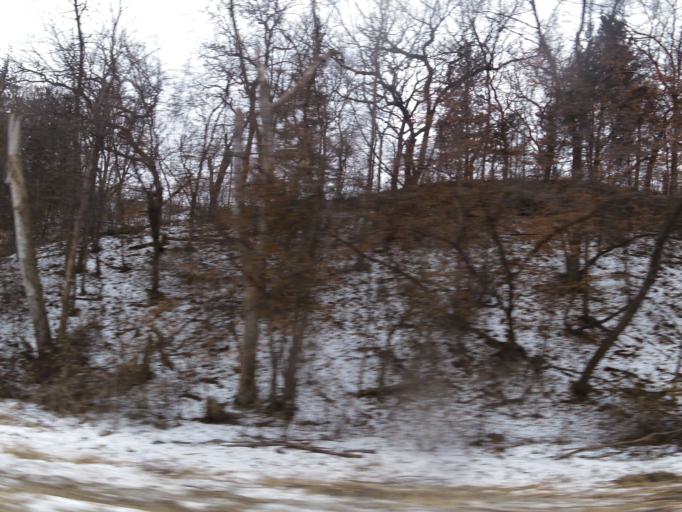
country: US
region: Minnesota
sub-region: Scott County
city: Jordan
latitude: 44.7053
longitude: -93.6475
